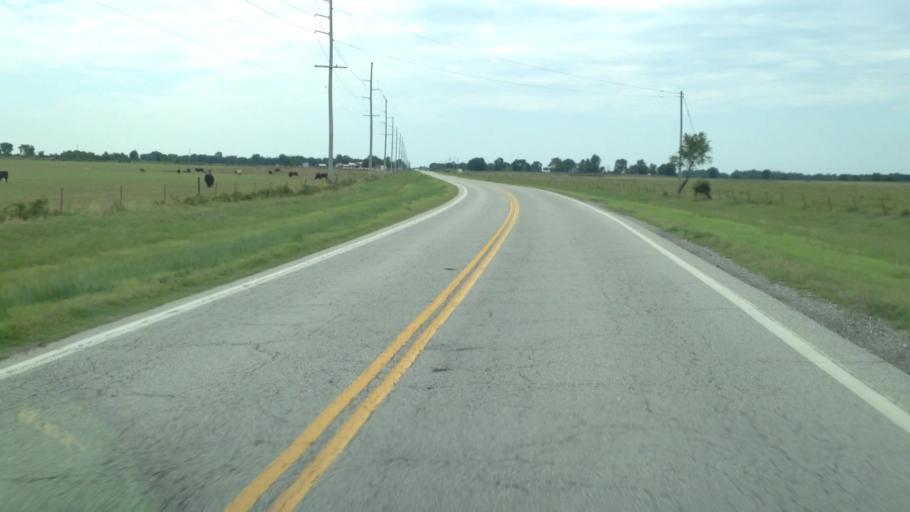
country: US
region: Kansas
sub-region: Labette County
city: Chetopa
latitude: 36.8971
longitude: -95.0897
